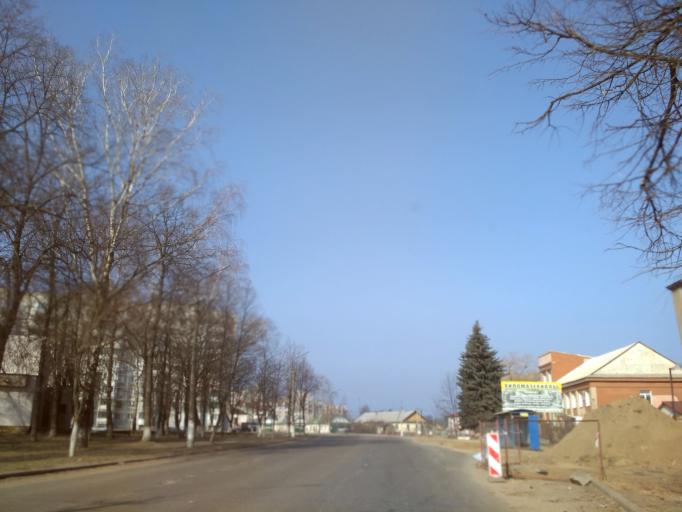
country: BY
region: Minsk
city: Horad Barysaw
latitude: 54.2284
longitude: 28.5164
